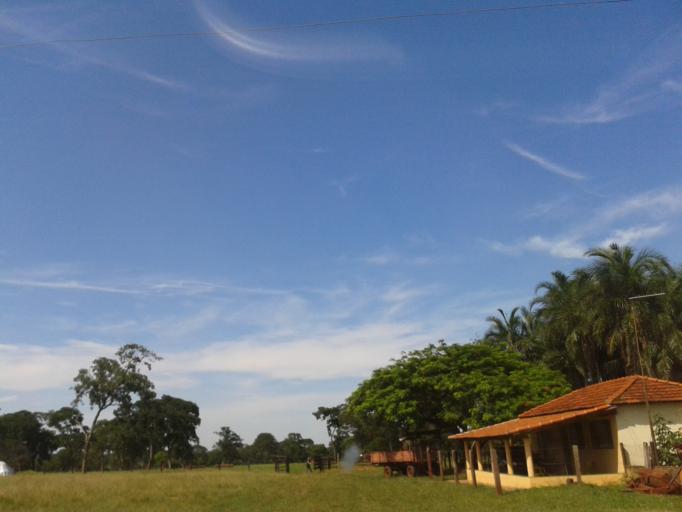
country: BR
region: Minas Gerais
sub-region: Santa Vitoria
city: Santa Vitoria
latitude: -19.1598
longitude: -50.5051
